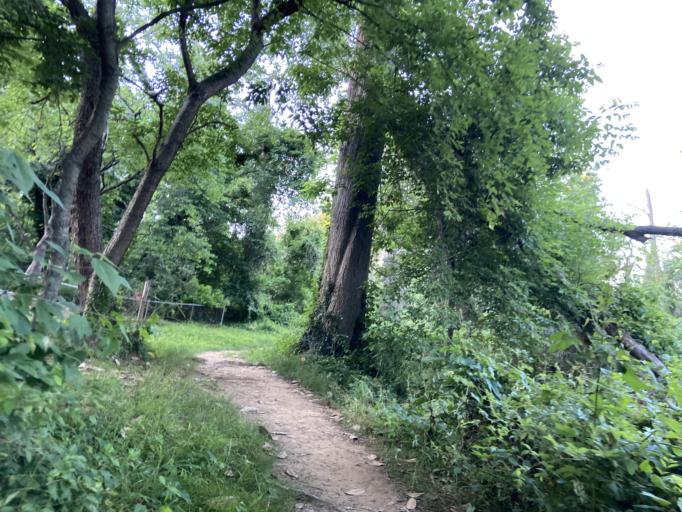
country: US
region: Virginia
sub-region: Fairfax County
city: McLean
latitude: 38.9173
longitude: -77.1760
